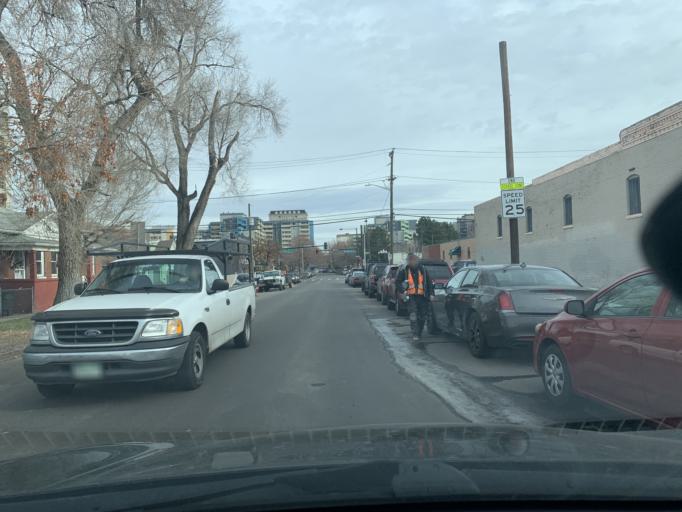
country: US
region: Colorado
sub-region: Denver County
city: Denver
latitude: 39.7353
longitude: -104.9999
